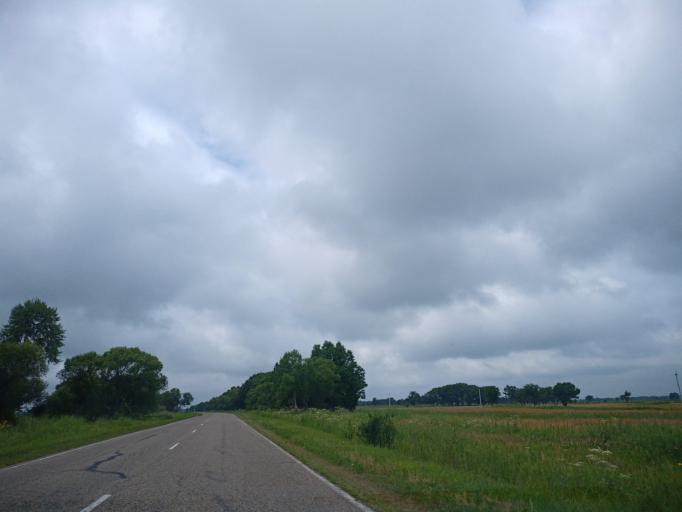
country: RU
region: Primorskiy
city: Dal'nerechensk
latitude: 45.9512
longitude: 133.9236
